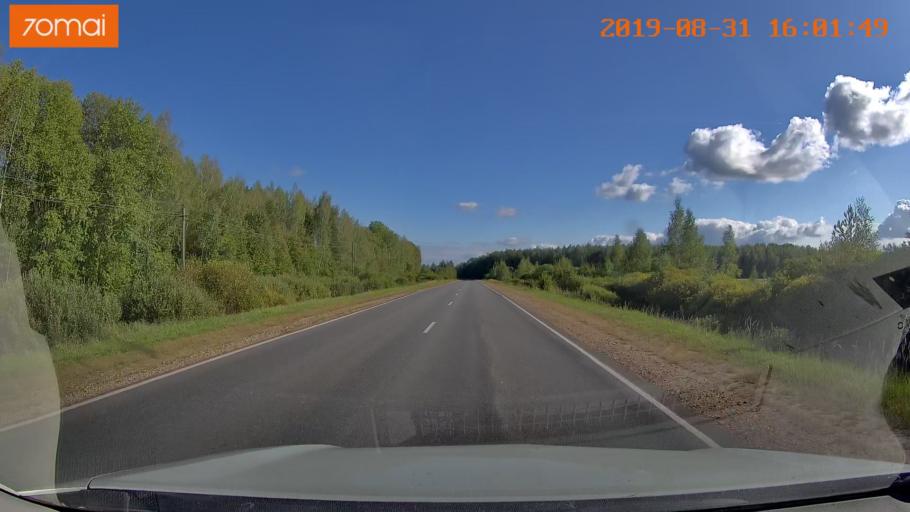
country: RU
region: Kaluga
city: Yukhnov
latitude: 54.6837
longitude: 35.2940
